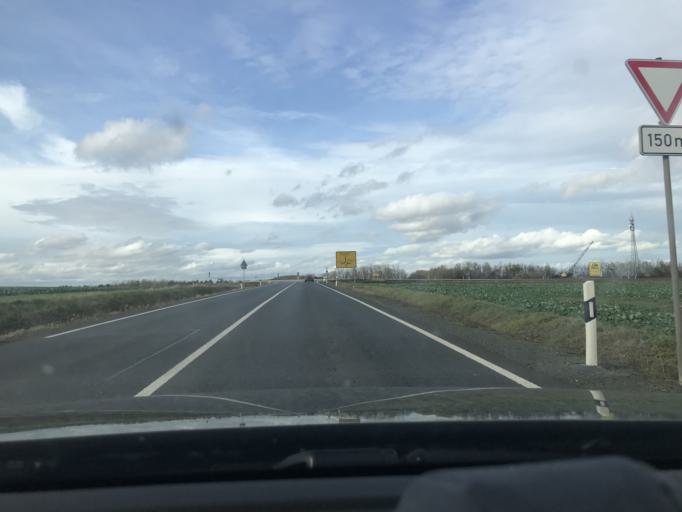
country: DE
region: Thuringia
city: Hochheim
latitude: 51.0516
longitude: 10.6554
